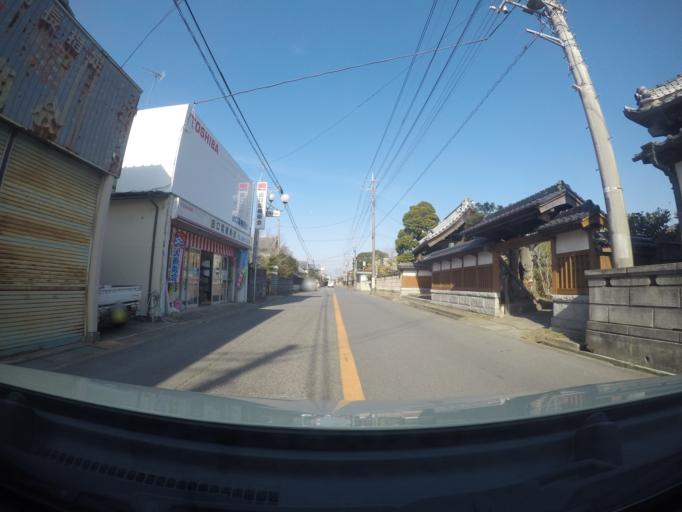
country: JP
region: Ibaraki
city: Tsukuba
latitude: 36.2219
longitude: 140.0662
